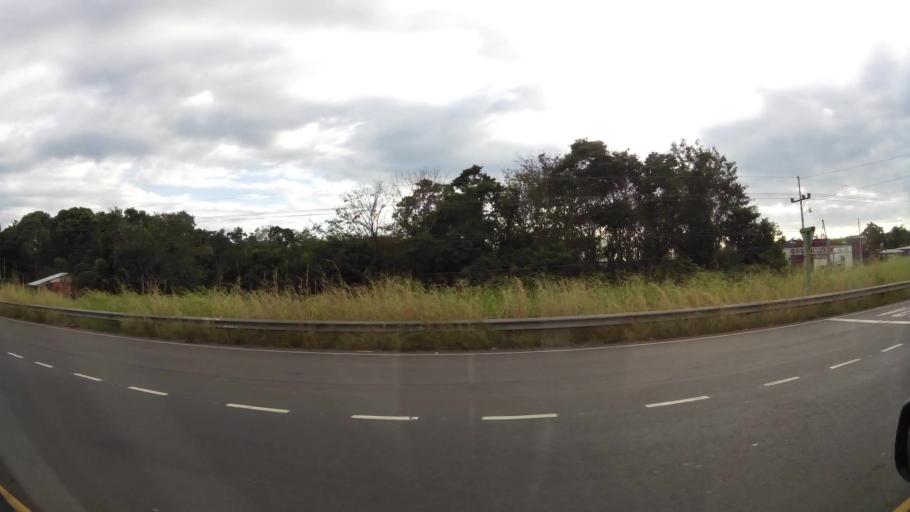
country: CR
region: Puntarenas
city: Esparza
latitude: 9.9065
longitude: -84.6632
